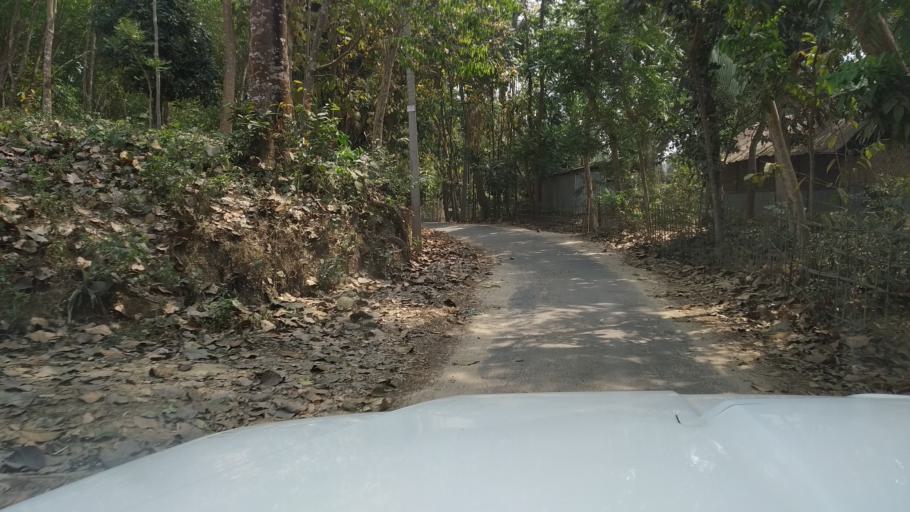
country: IN
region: Tripura
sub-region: West Tripura
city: Sonamura
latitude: 23.4301
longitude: 91.3133
